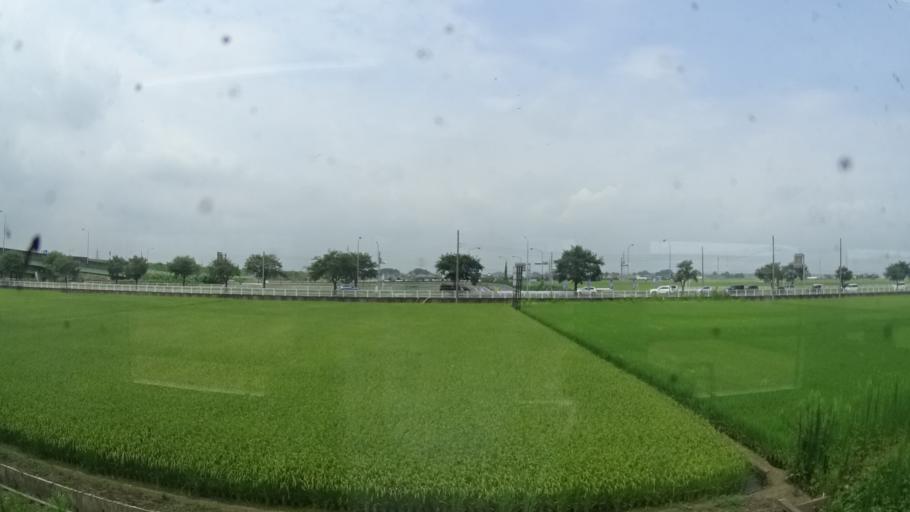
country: JP
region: Ibaraki
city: Shimodate
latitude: 36.3268
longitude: 139.9708
